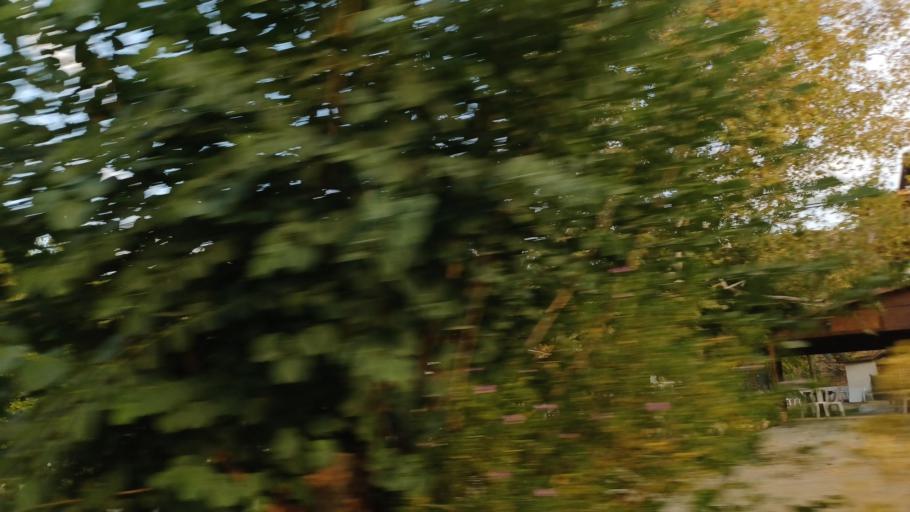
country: CY
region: Lefkosia
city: Kakopetria
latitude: 35.0349
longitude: 32.9021
